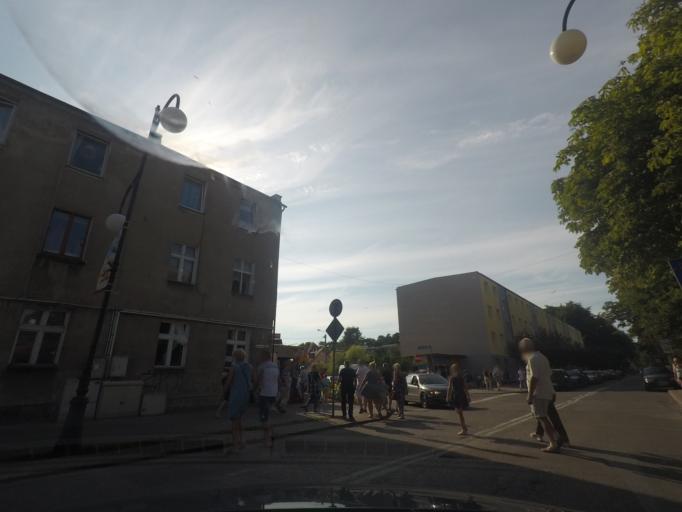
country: PL
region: Pomeranian Voivodeship
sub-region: Powiat leborski
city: Leba
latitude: 54.7613
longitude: 17.5536
